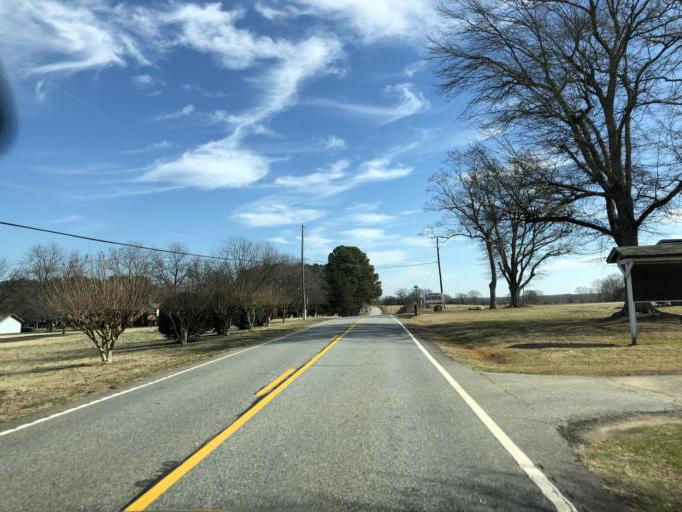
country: US
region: South Carolina
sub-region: Spartanburg County
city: Mayo
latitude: 35.0513
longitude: -81.9162
